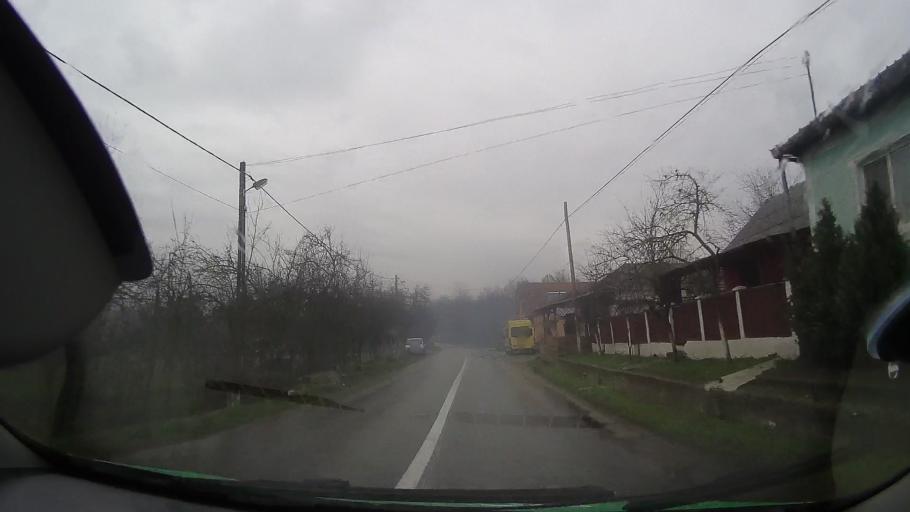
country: RO
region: Bihor
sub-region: Comuna Holod
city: Vintere
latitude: 46.7711
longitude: 22.1378
